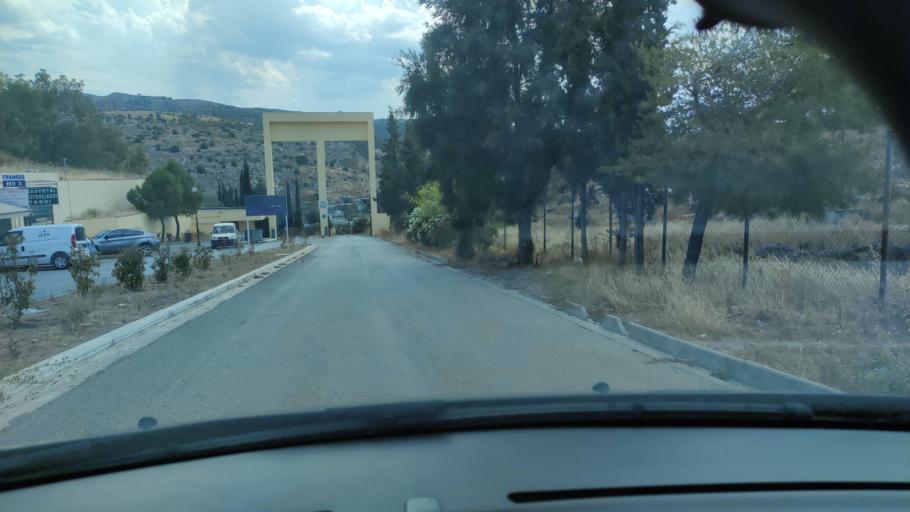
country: GR
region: Attica
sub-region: Nomos Piraios
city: Keratsini
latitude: 37.9792
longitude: 23.6000
